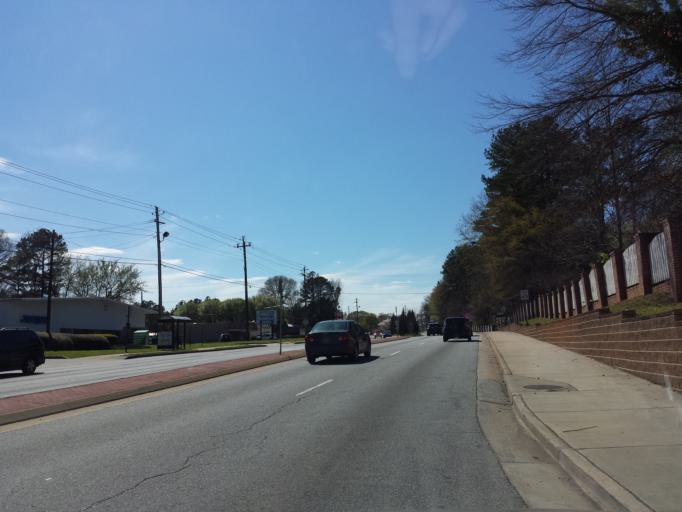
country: US
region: Georgia
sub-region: Cobb County
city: Smyrna
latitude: 33.8837
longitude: -84.4991
